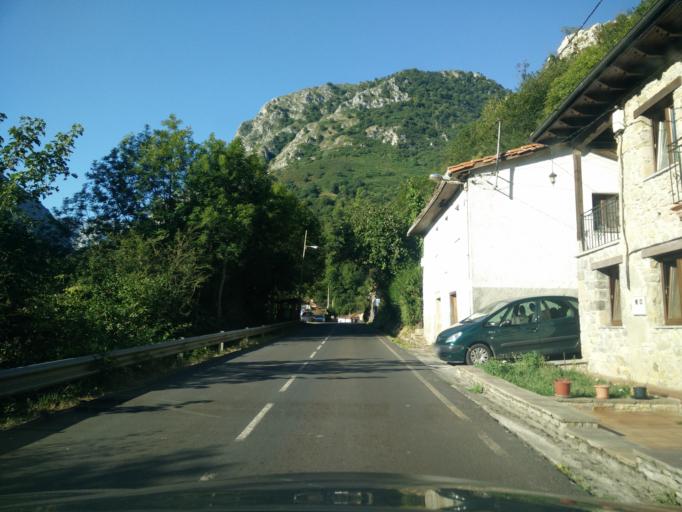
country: ES
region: Asturias
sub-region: Province of Asturias
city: Parres
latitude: 43.2590
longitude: -5.2003
